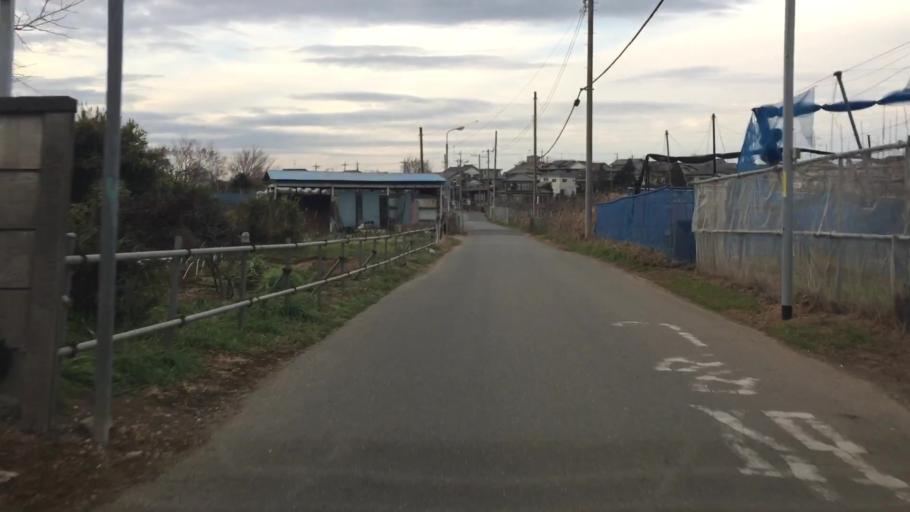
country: JP
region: Chiba
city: Shiroi
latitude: 35.7865
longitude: 139.9986
